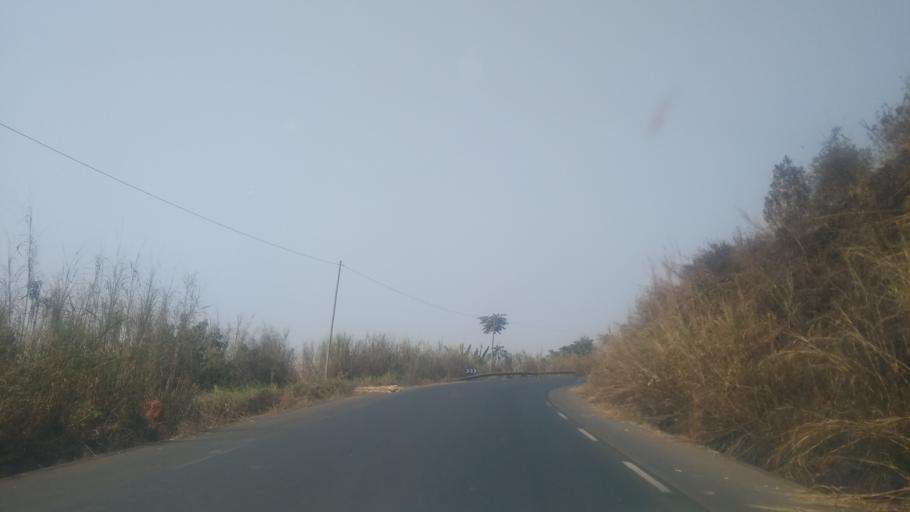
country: CM
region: West
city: Dschang
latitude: 5.4057
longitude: 10.0162
